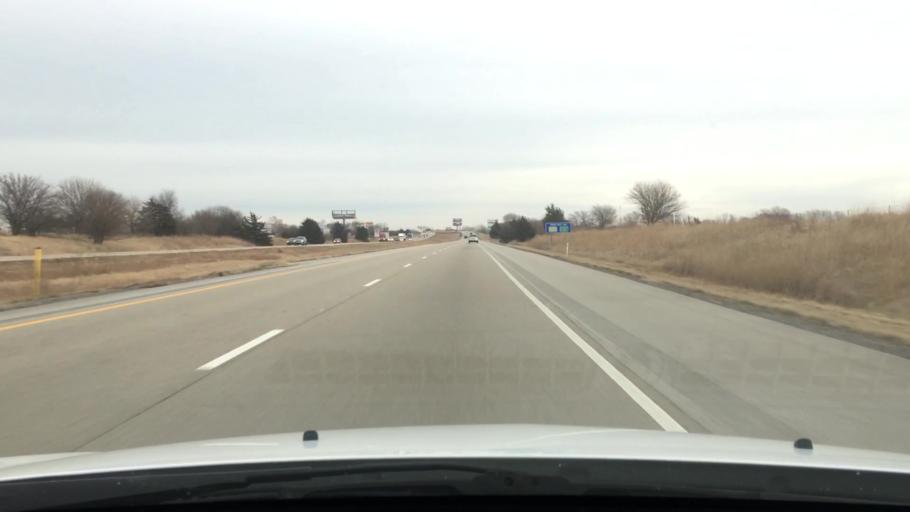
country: US
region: Illinois
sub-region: Logan County
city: Atlanta
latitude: 40.2501
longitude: -89.2397
